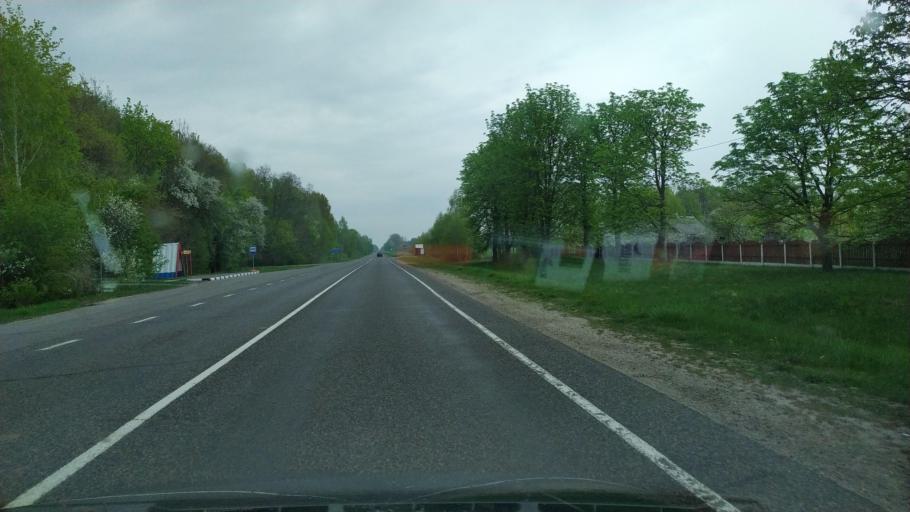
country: BY
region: Brest
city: Horad Kobryn
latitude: 52.2865
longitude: 24.4922
